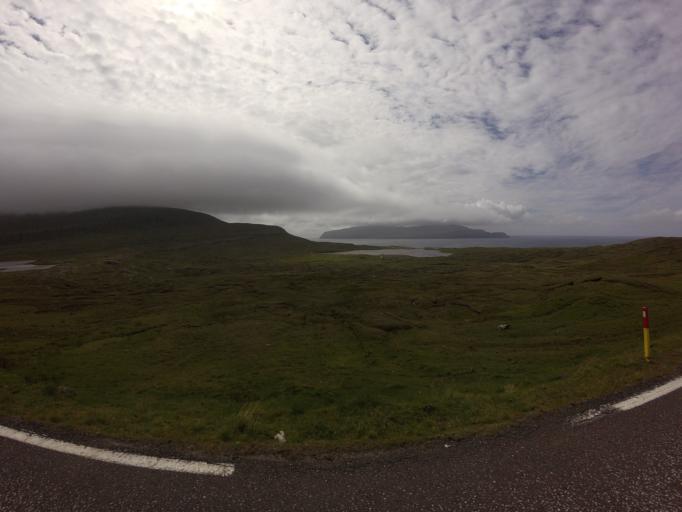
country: FO
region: Sandoy
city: Sandur
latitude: 61.8257
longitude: -6.7427
